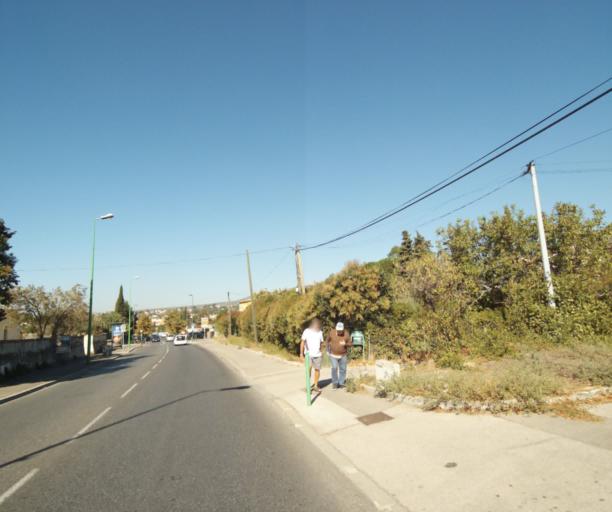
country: FR
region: Provence-Alpes-Cote d'Azur
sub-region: Departement des Bouches-du-Rhone
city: Plan-de-Cuques
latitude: 43.3422
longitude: 5.4709
